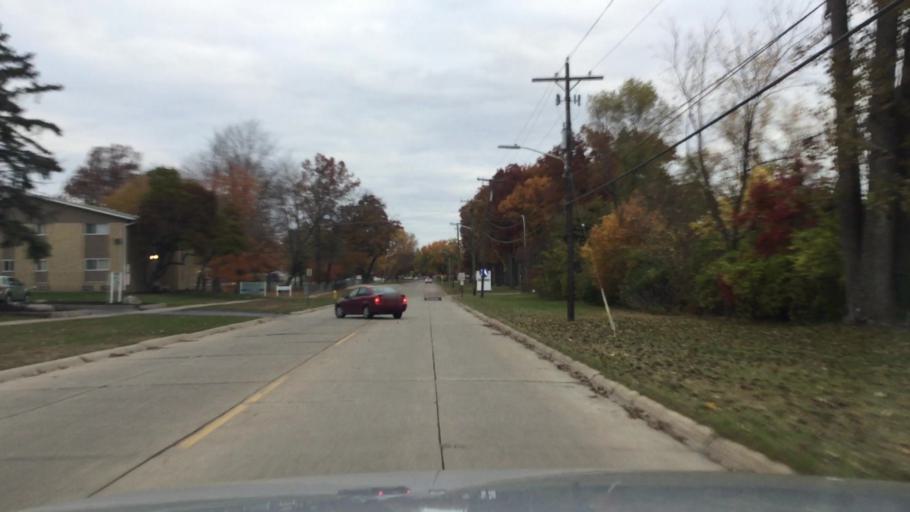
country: US
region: Michigan
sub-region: Wayne County
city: Westland
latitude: 42.3291
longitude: -83.3797
